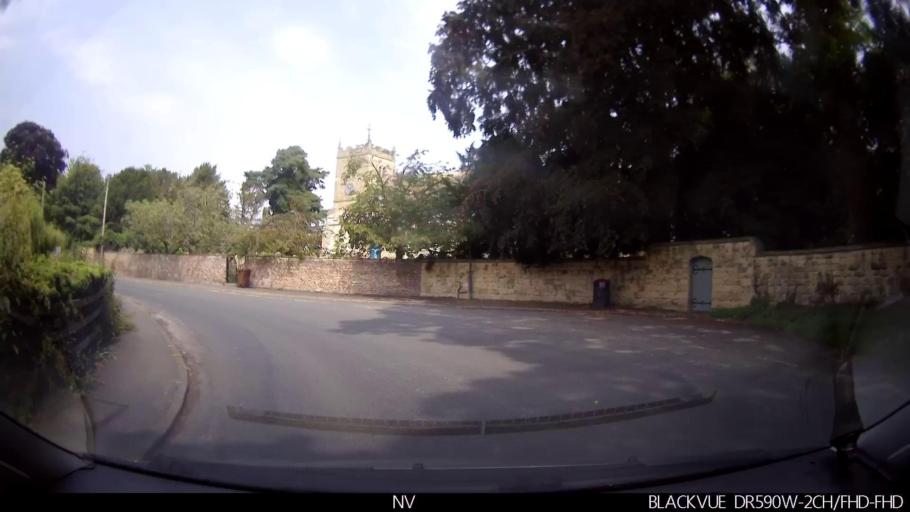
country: GB
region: England
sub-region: North Yorkshire
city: Great Habton
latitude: 54.2054
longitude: -0.8069
